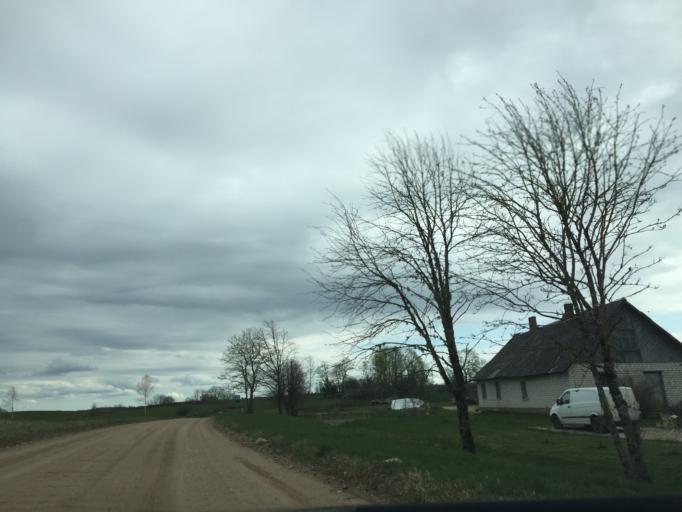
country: LV
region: Jaunpiebalga
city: Jaunpiebalga
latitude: 57.1421
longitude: 25.9434
